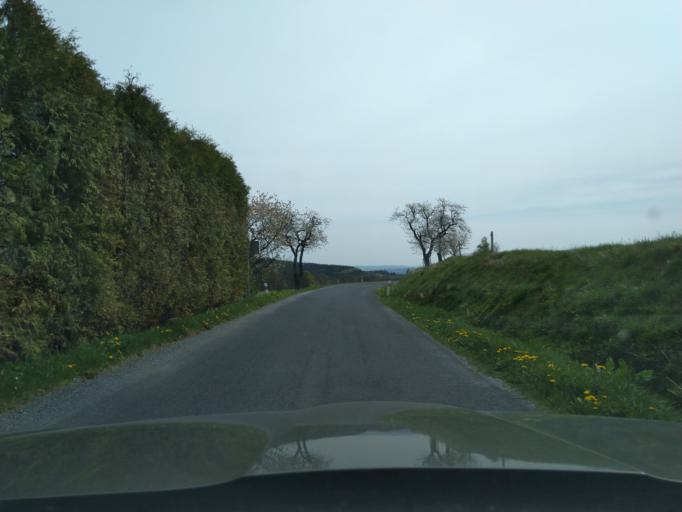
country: CZ
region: Jihocesky
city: Vacov
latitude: 49.1734
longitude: 13.6791
